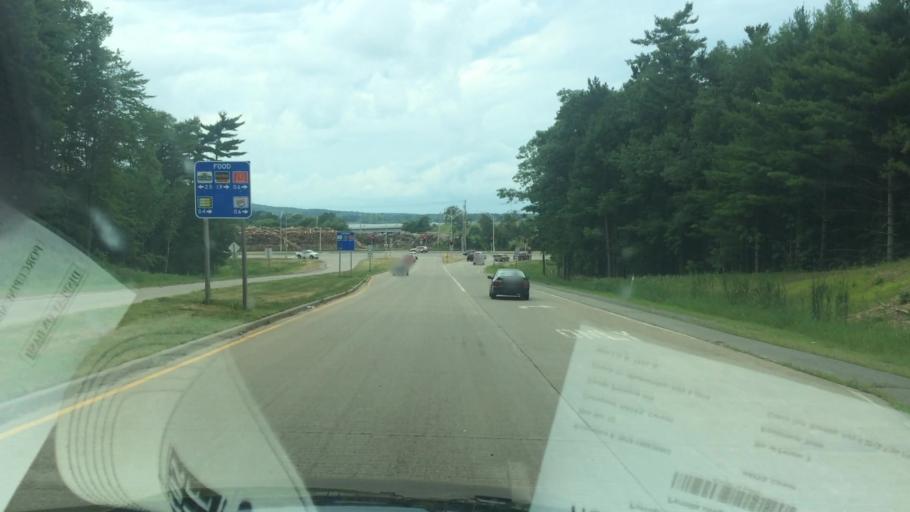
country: US
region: Wisconsin
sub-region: Marathon County
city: Rothschild
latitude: 44.8942
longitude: -89.6140
